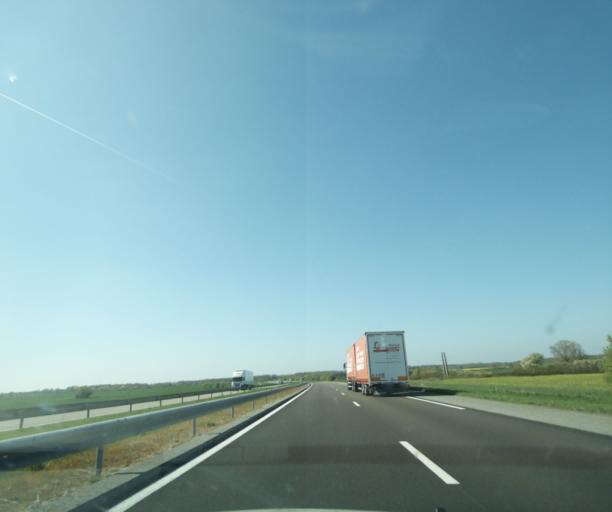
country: FR
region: Centre
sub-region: Departement du Loiret
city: Briare
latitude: 47.6321
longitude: 2.7841
